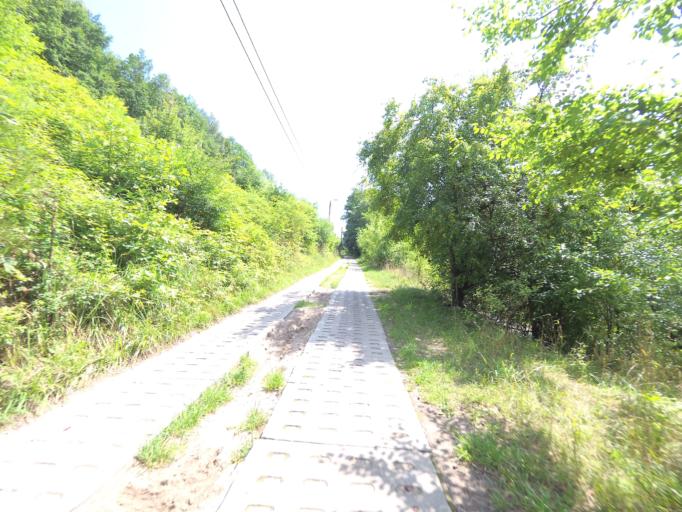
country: PL
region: Pomeranian Voivodeship
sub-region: Gdynia
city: Wielki Kack
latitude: 54.4875
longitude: 18.5060
